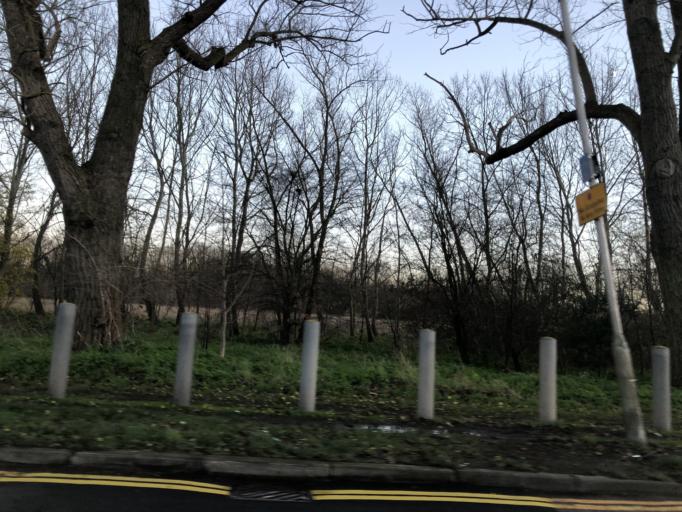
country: GB
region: England
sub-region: Greater London
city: Woolwich
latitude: 51.4753
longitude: 0.0488
